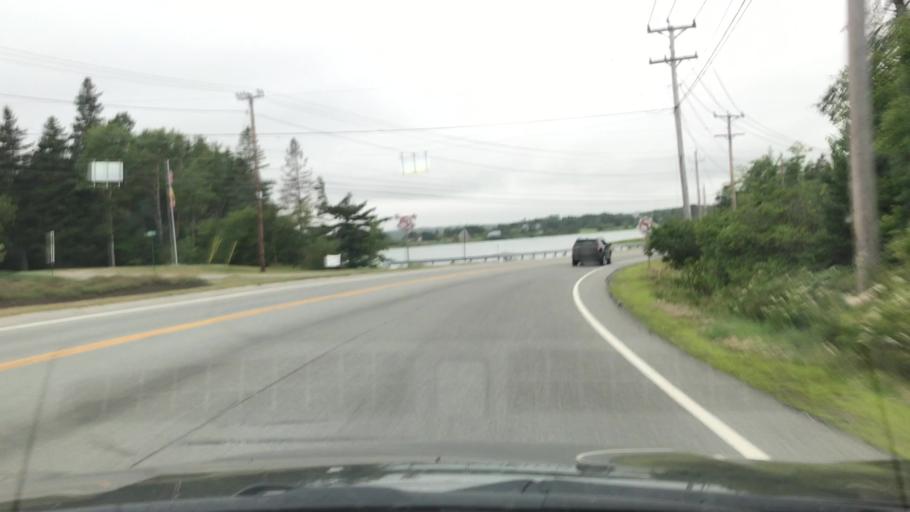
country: US
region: Maine
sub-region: Hancock County
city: Trenton
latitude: 44.4215
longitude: -68.3633
